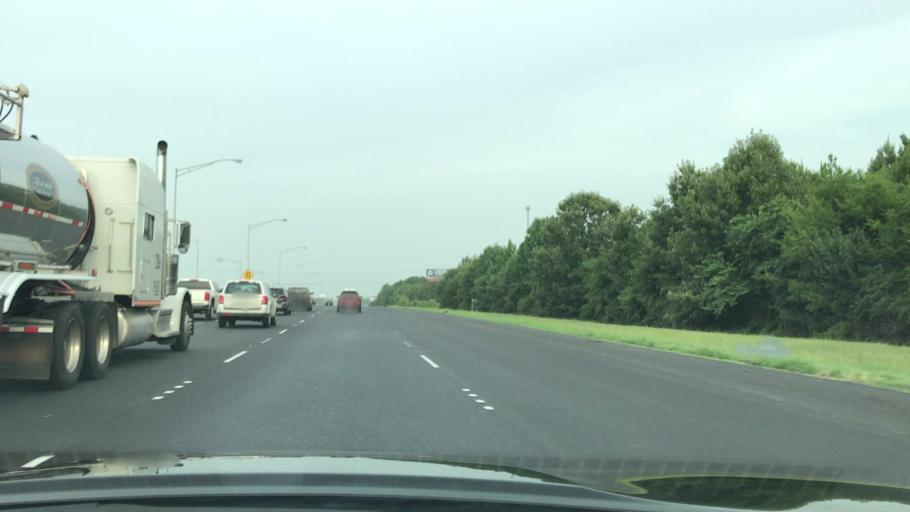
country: US
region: Louisiana
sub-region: Caddo Parish
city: Greenwood
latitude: 32.4498
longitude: -93.8717
